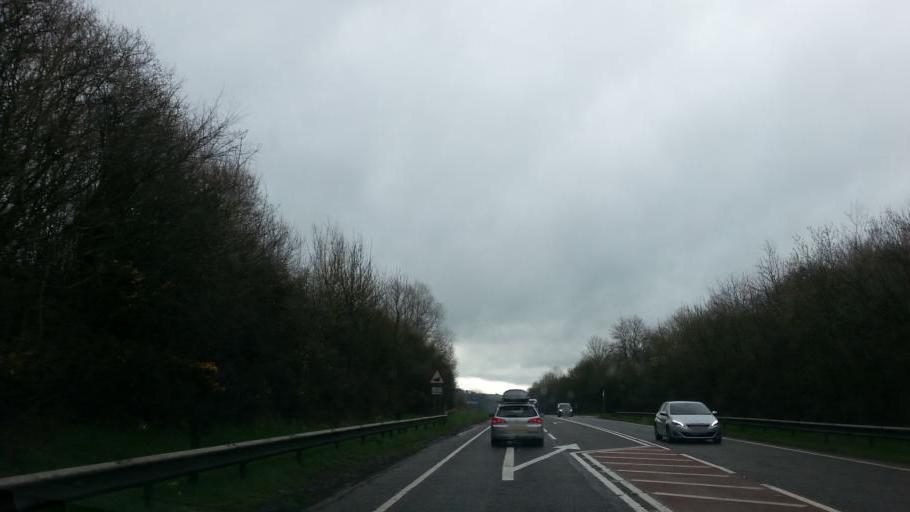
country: GB
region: England
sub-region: Devon
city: South Molton
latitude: 51.0489
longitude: -3.9197
